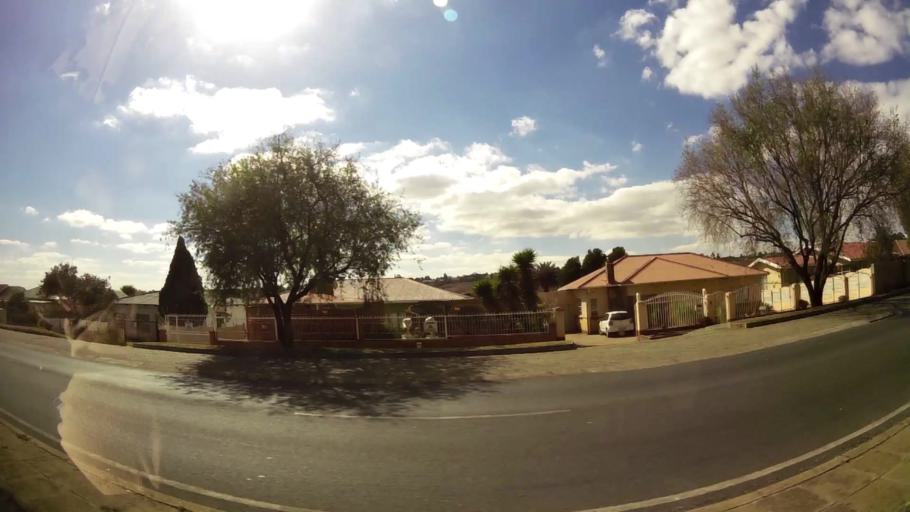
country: ZA
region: Gauteng
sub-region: West Rand District Municipality
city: Krugersdorp
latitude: -26.1129
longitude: 27.7938
